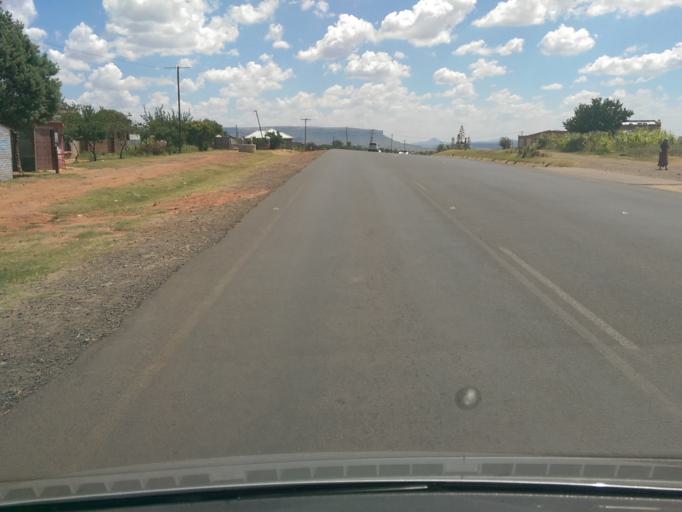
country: LS
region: Maseru
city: Maseru
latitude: -29.4089
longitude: 27.5829
